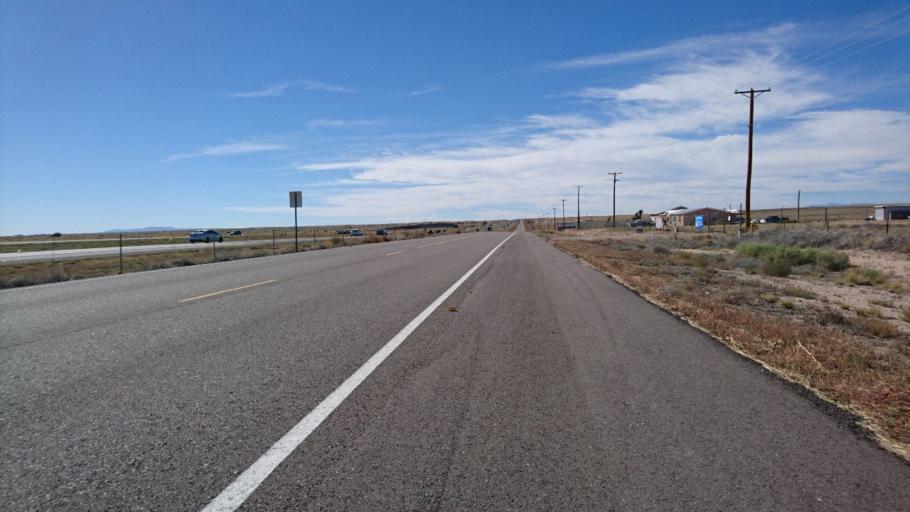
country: US
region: New Mexico
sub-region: Bernalillo County
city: South Valley
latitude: 35.0572
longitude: -106.8255
